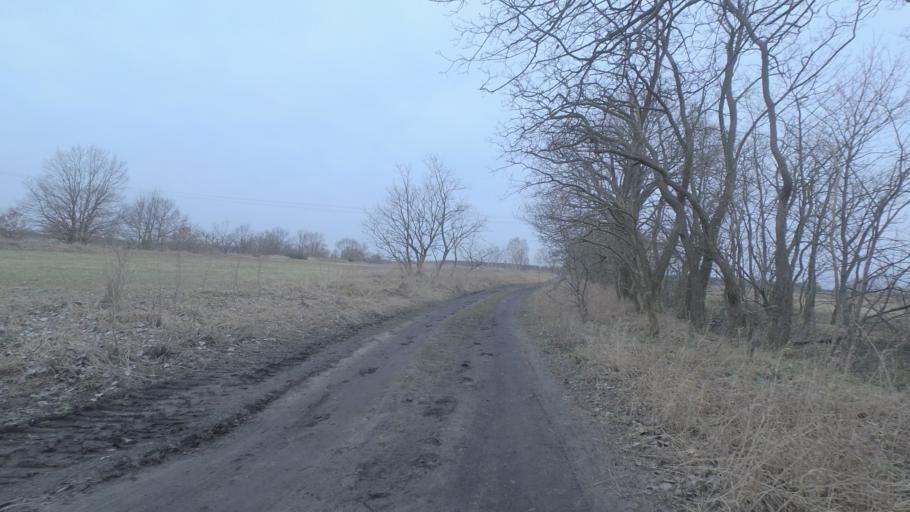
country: DE
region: Brandenburg
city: Ludwigsfelde
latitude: 52.3257
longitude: 13.2301
